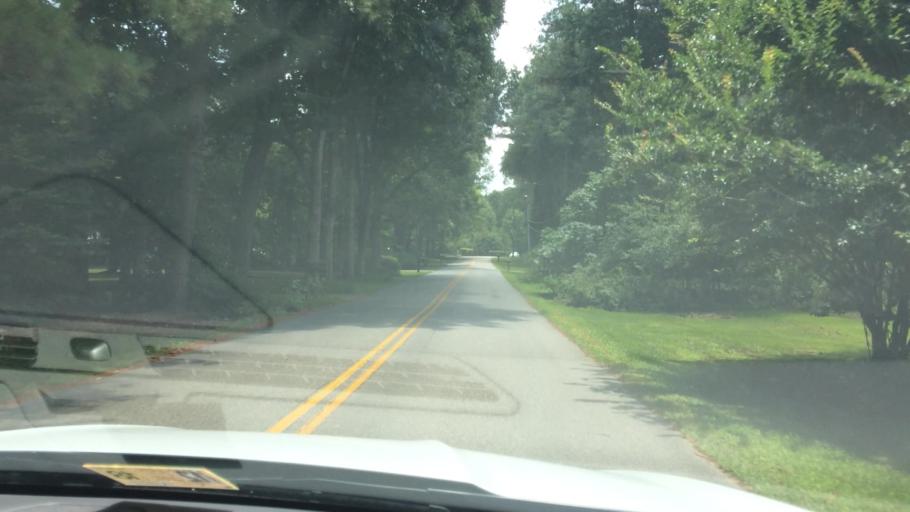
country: US
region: Virginia
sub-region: York County
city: Yorktown
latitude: 37.2058
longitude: -76.4831
